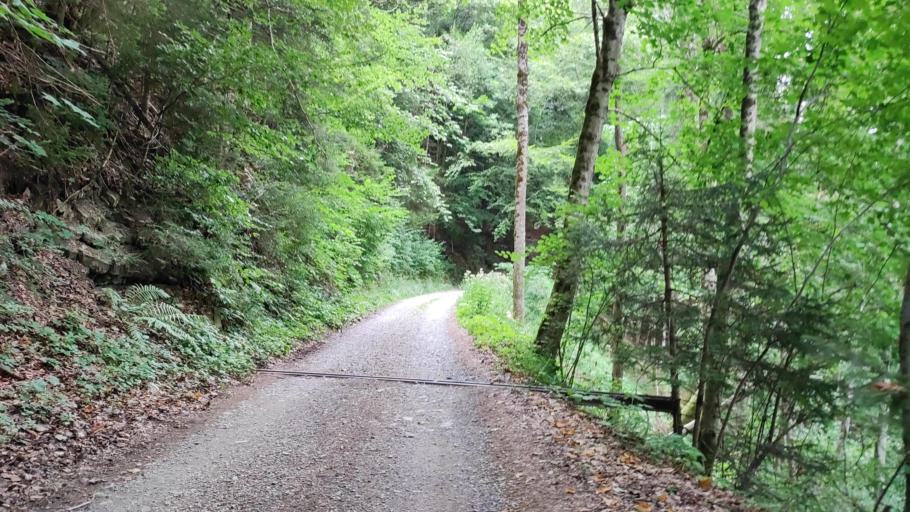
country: AT
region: Vorarlberg
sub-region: Politischer Bezirk Feldkirch
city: Feldkirch
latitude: 47.2035
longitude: 9.6091
